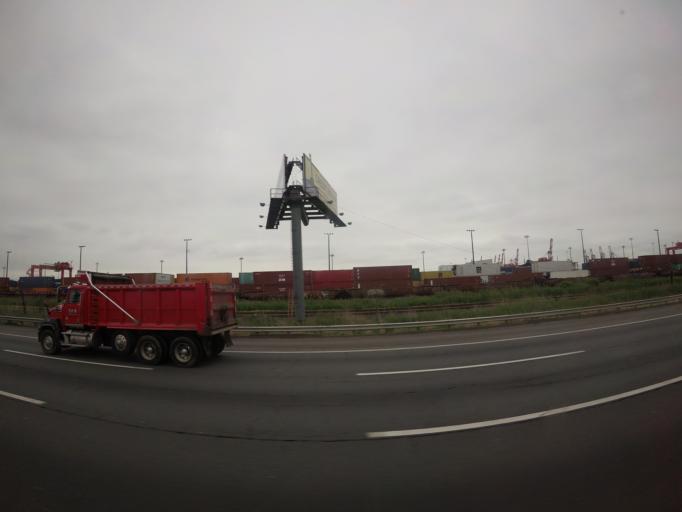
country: US
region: New Jersey
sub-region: Essex County
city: Newark
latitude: 40.6942
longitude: -74.1589
